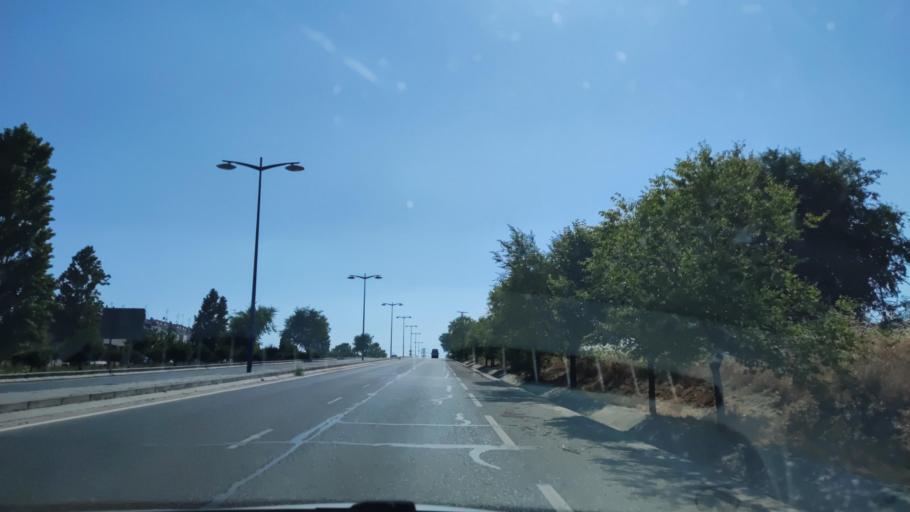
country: ES
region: Madrid
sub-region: Provincia de Madrid
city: Leganes
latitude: 40.3455
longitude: -3.7817
